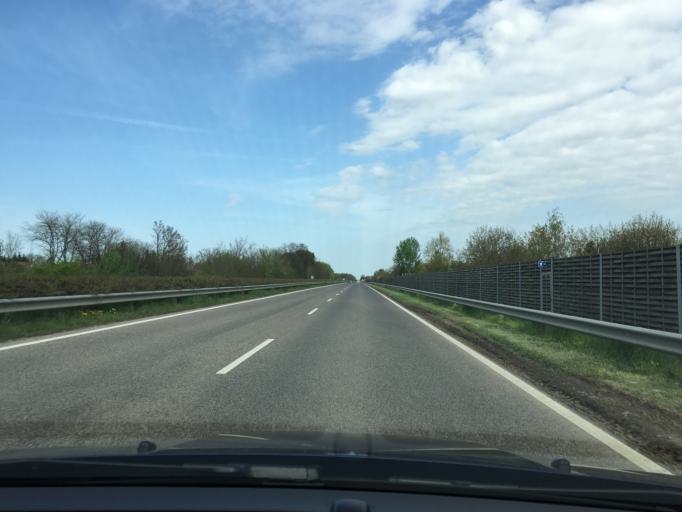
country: HU
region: Csongrad
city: Hodmezovasarhely
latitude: 46.3915
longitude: 20.2819
